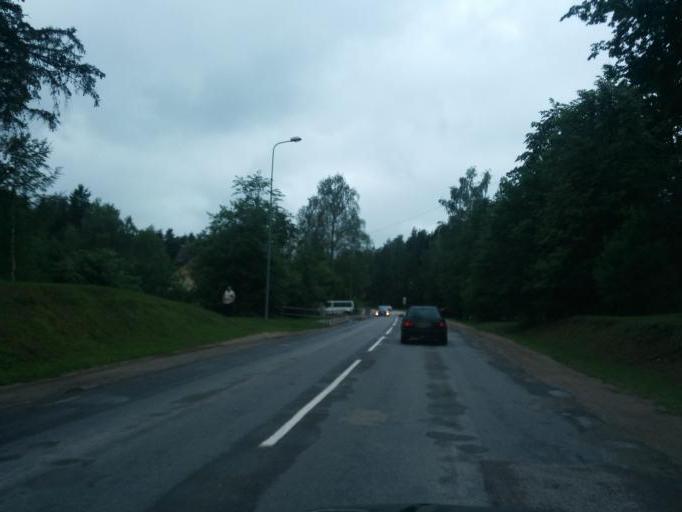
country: LV
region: Smiltene
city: Smiltene
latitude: 57.4193
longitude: 25.9253
